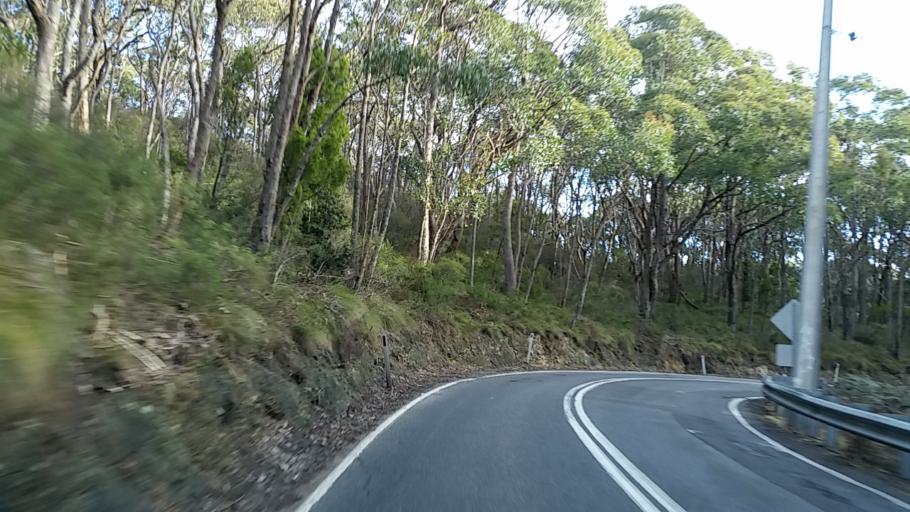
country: AU
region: South Australia
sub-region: Adelaide Hills
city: Bridgewater
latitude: -34.9630
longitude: 138.7550
